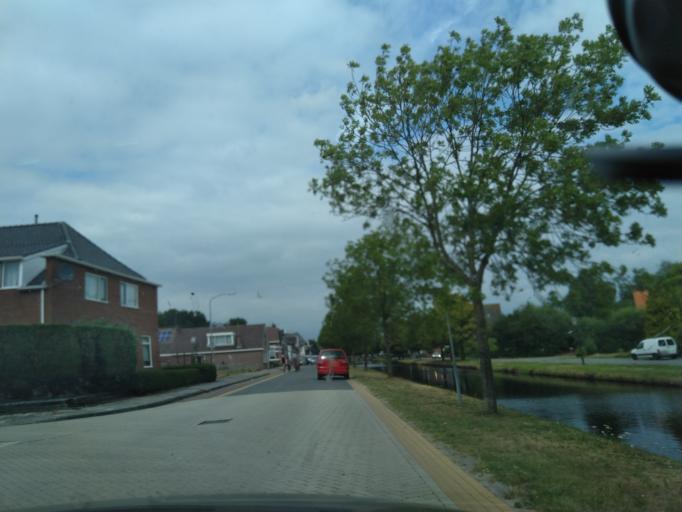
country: NL
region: Groningen
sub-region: Gemeente Pekela
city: Oude Pekela
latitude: 53.0945
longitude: 6.9900
